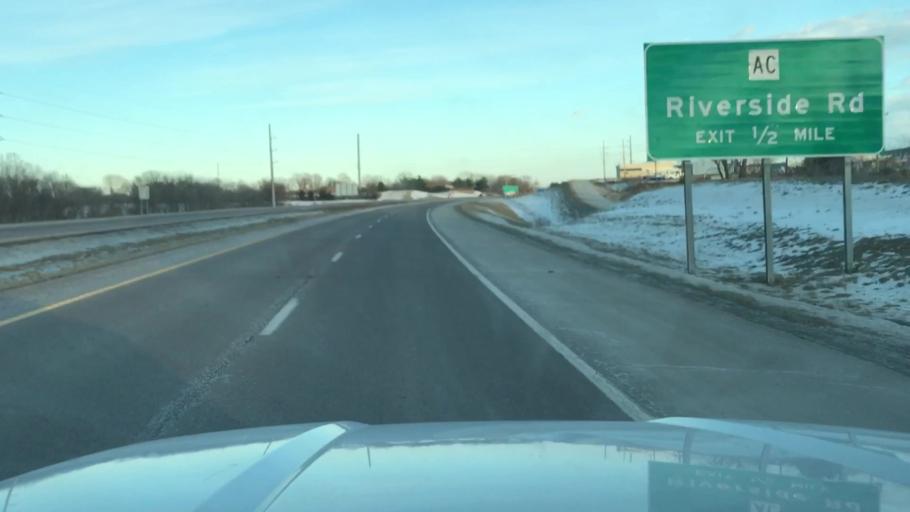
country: US
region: Missouri
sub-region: Buchanan County
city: Saint Joseph
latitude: 39.7515
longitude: -94.7801
